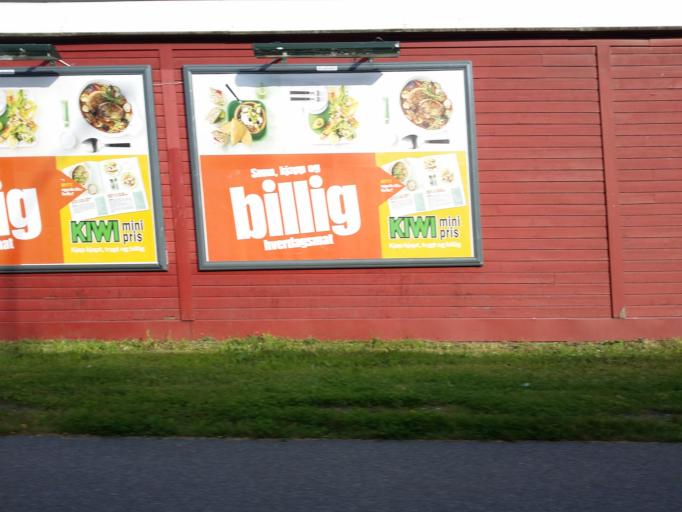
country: NO
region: Akershus
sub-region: Oppegard
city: Kolbotn
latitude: 59.8913
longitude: 10.8548
